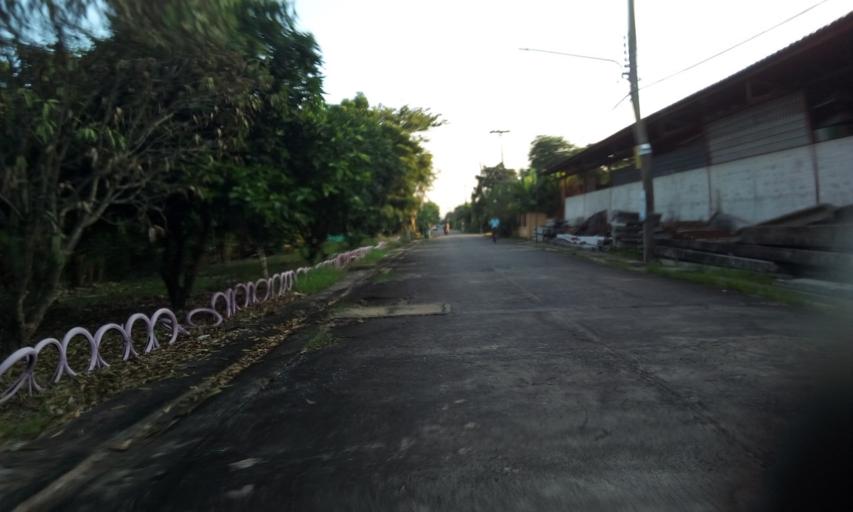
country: TH
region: Pathum Thani
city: Ban Rangsit
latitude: 14.0501
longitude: 100.8225
